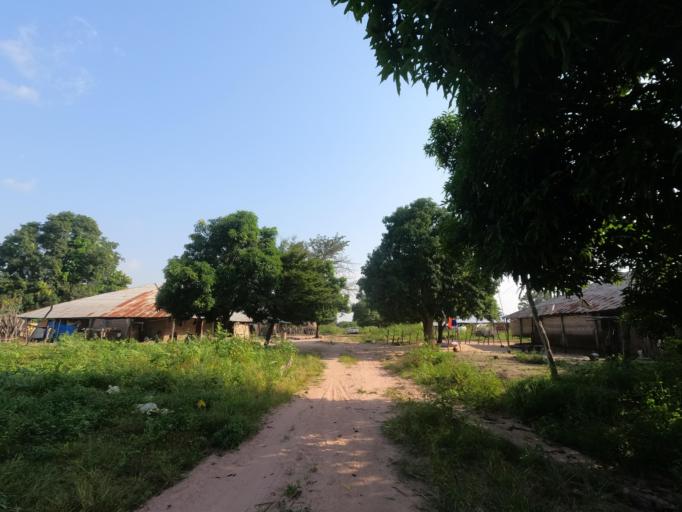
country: SN
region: Sedhiou
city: Sedhiou
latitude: 12.4218
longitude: -15.7332
